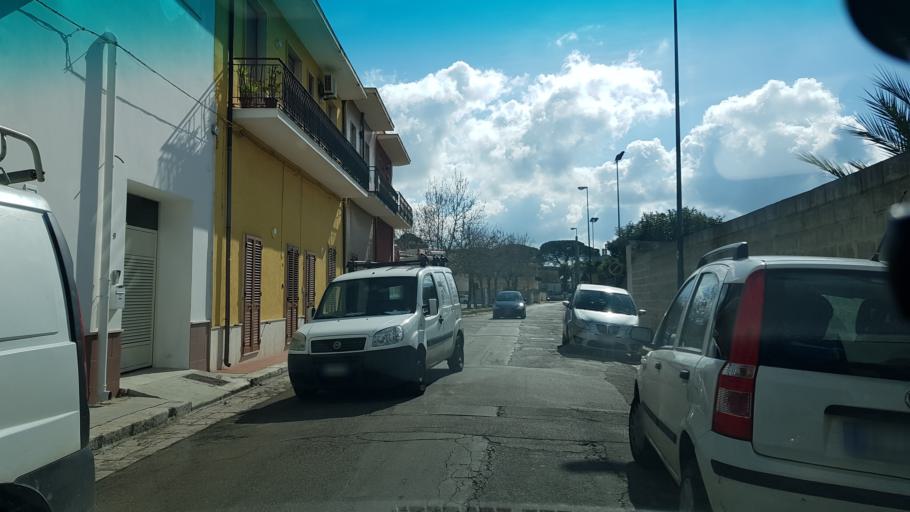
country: IT
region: Apulia
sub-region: Provincia di Lecce
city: Campi Salentina
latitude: 40.3955
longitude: 18.0171
